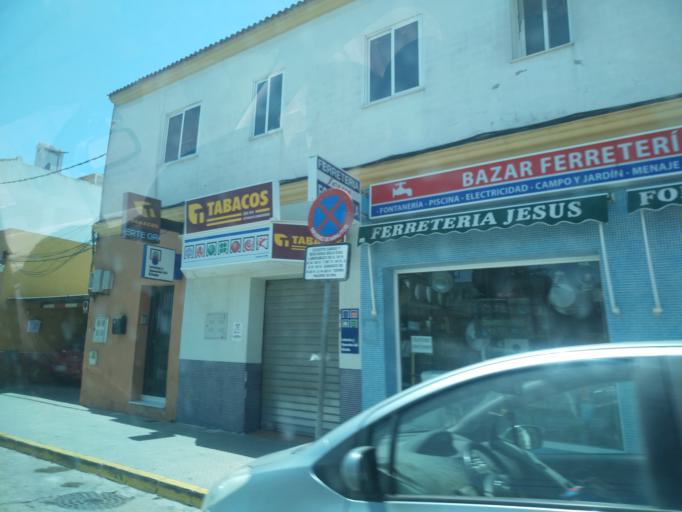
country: ES
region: Andalusia
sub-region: Provincia de Cadiz
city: Chiclana de la Frontera
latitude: 36.4104
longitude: -6.1663
